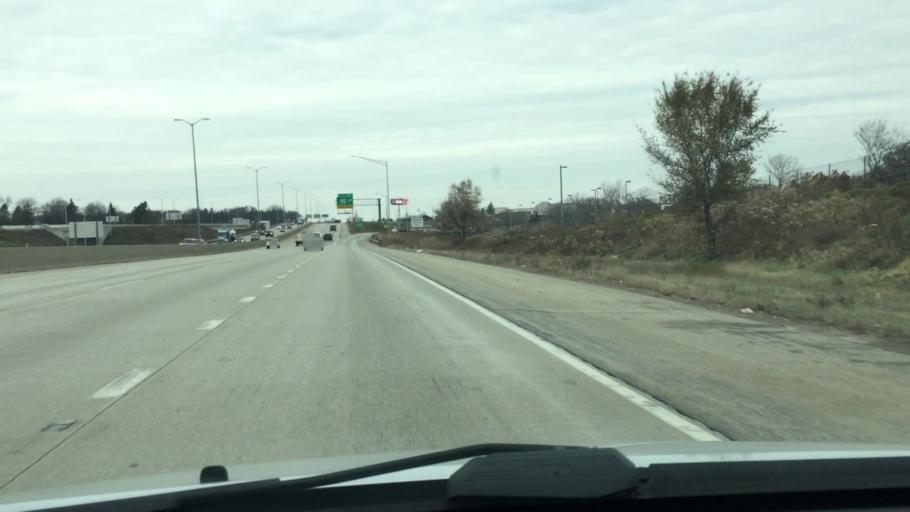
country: US
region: Wisconsin
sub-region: Waukesha County
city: Butler
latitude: 43.1571
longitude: -88.0594
